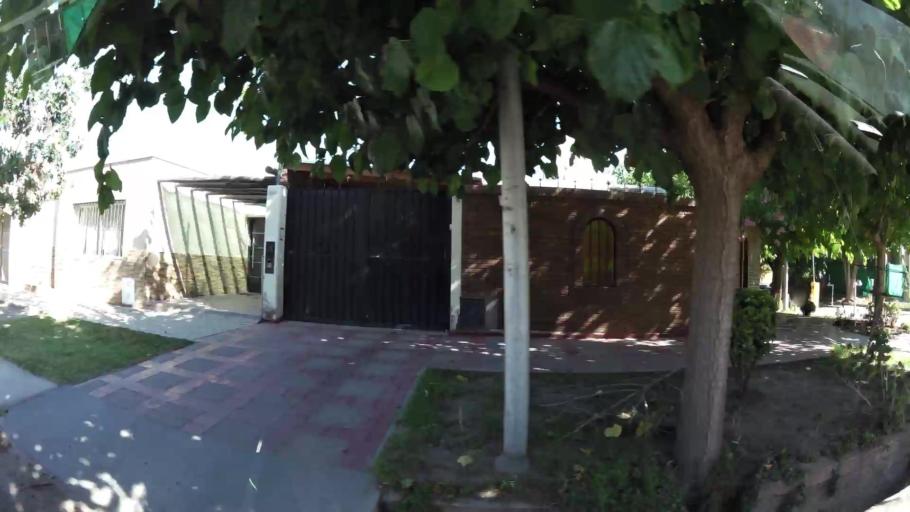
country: AR
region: Mendoza
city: Villa Nueva
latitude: -32.9106
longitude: -68.7911
